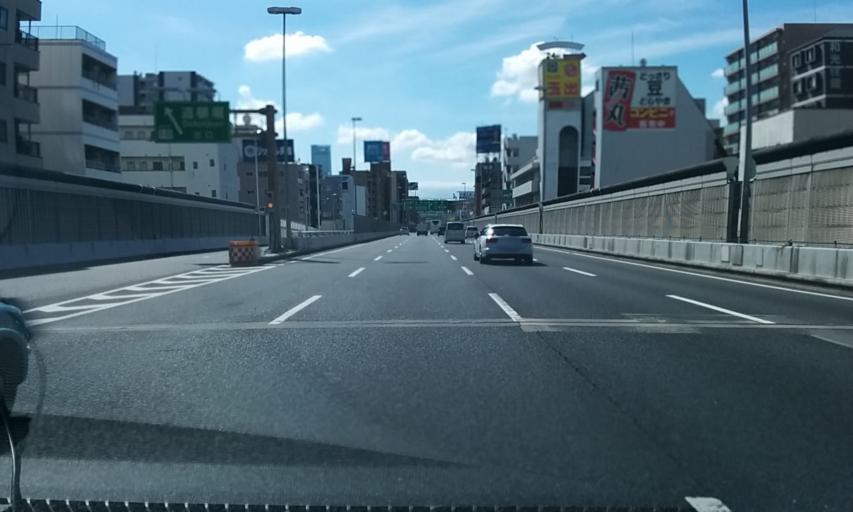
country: JP
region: Osaka
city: Osaka-shi
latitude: 34.6718
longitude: 135.5107
